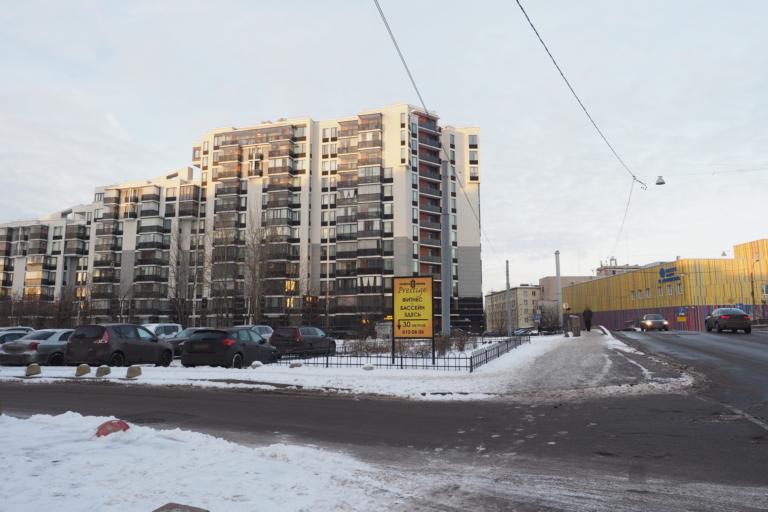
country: RU
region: St.-Petersburg
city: Novaya Derevnya
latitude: 59.9681
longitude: 30.2888
